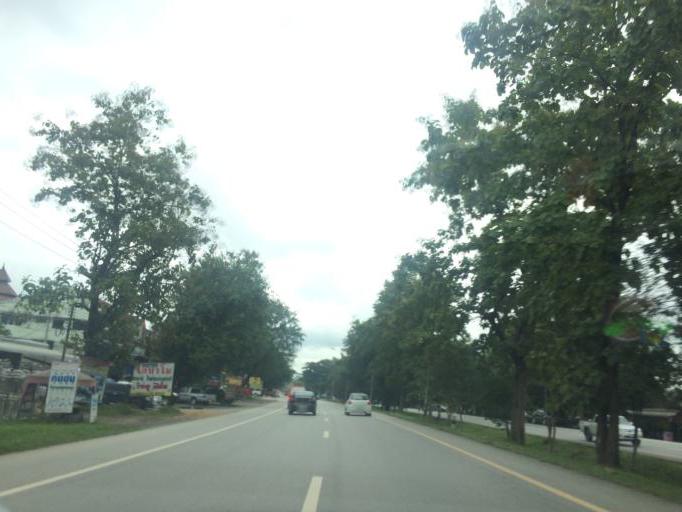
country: TH
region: Chiang Rai
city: Chiang Rai
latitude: 19.8627
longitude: 99.8212
